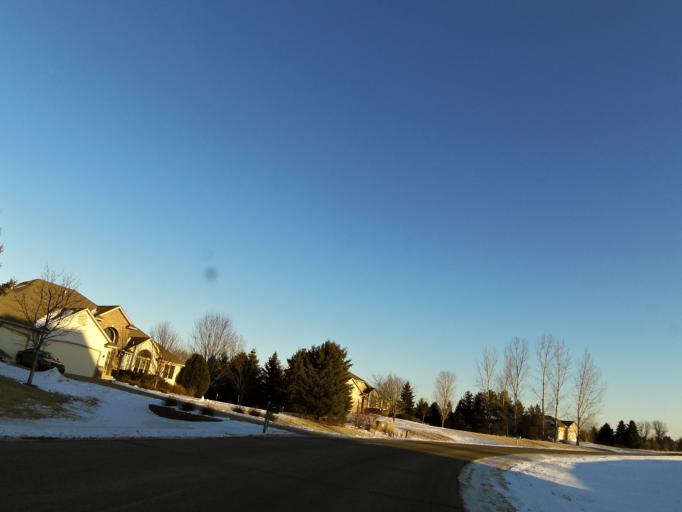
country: US
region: Minnesota
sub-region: Washington County
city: Lake Elmo
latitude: 44.9881
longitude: -92.8568
